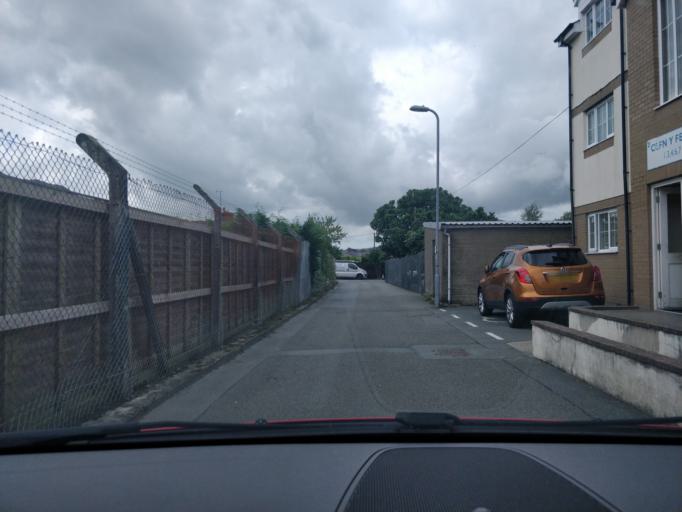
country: GB
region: Wales
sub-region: Gwynedd
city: Porthmadog
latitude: 52.9291
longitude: -4.1290
